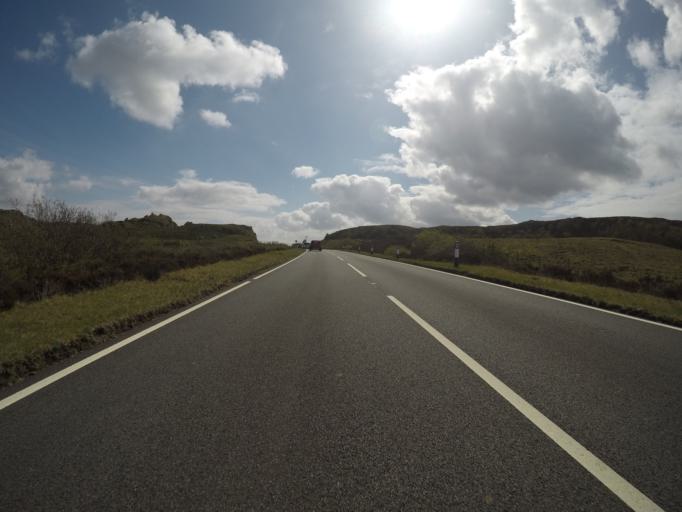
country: GB
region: Scotland
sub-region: Highland
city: Portree
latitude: 57.5171
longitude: -6.3420
